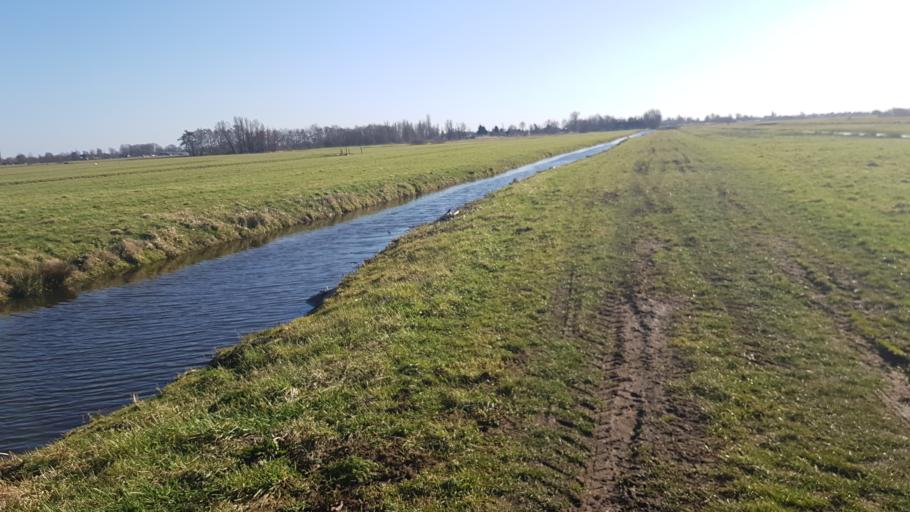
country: NL
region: South Holland
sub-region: Molenwaard
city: Nieuw-Lekkerland
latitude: 51.9260
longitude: 4.7508
